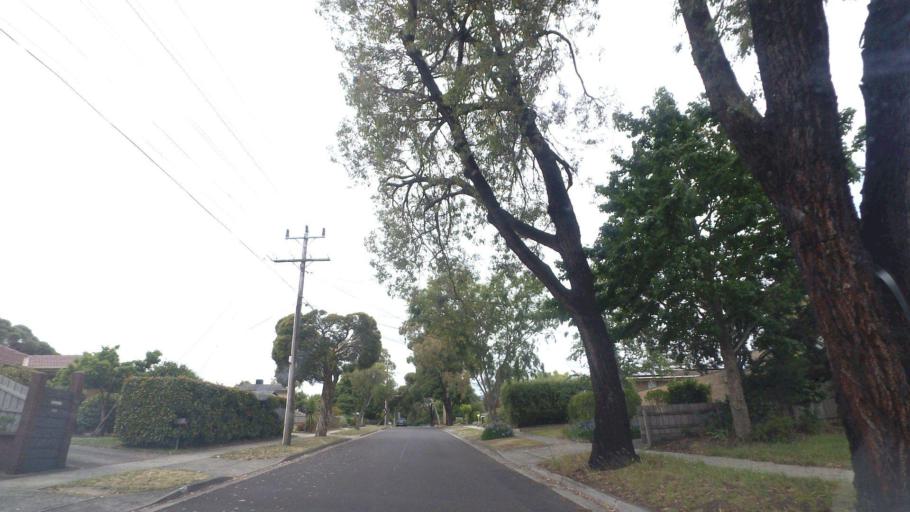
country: AU
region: Victoria
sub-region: Knox
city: The Basin
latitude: -37.8531
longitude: 145.3071
